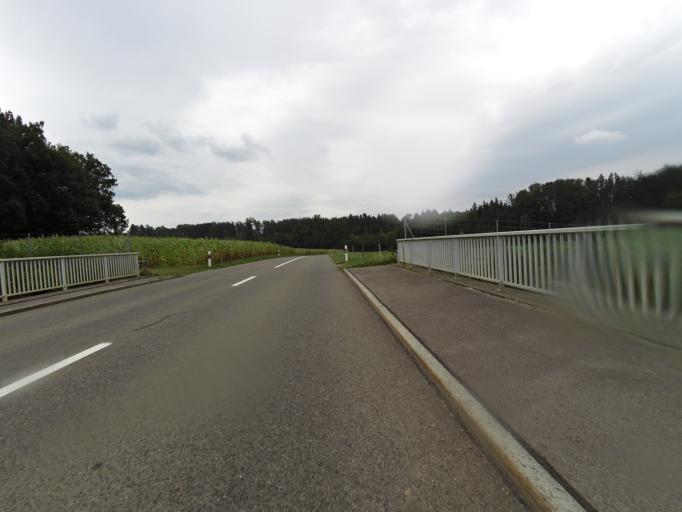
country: CH
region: Thurgau
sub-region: Weinfelden District
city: Wigoltingen
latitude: 47.6079
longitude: 9.0385
